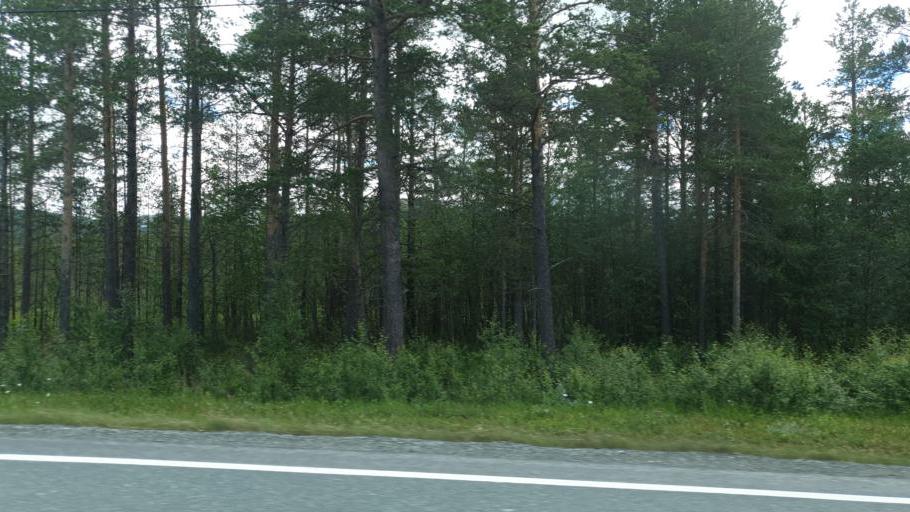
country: NO
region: Sor-Trondelag
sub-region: Oppdal
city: Oppdal
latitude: 62.6531
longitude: 9.8684
